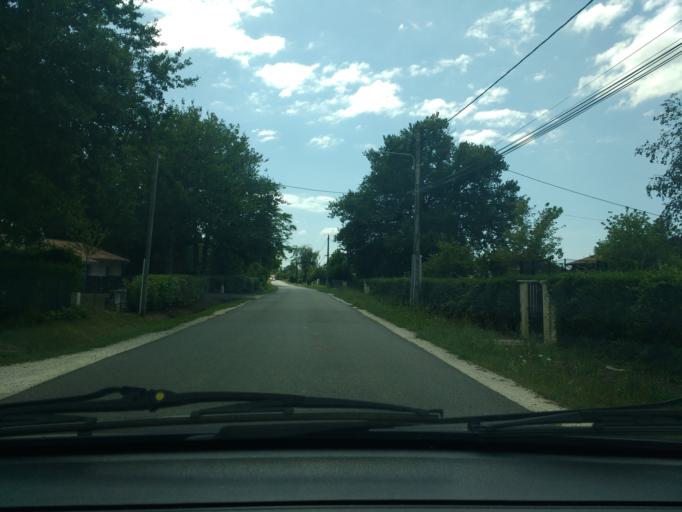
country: FR
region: Aquitaine
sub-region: Departement de la Gironde
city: Salles
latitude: 44.5620
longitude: -0.8480
